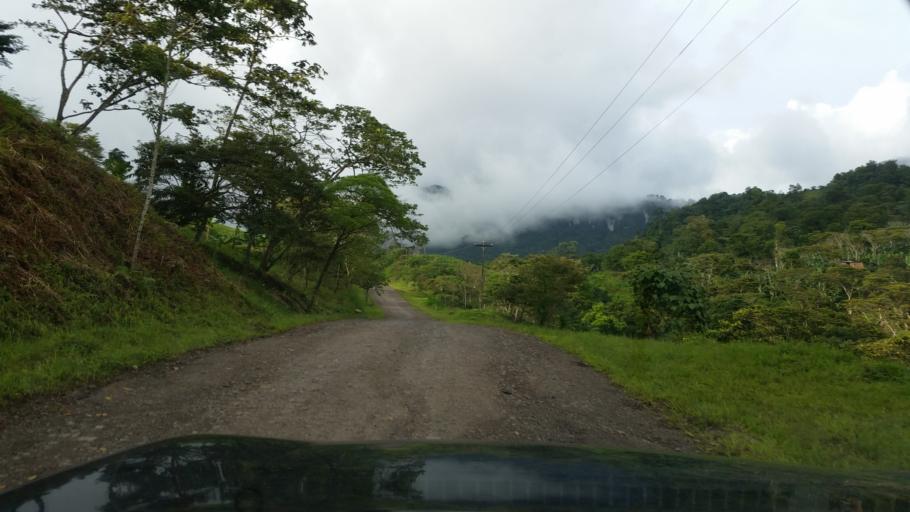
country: NI
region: Jinotega
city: Jinotega
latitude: 13.2652
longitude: -85.7315
